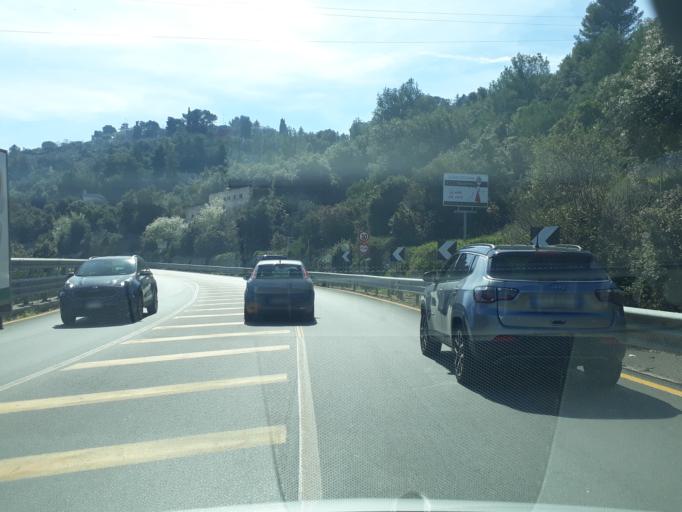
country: IT
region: Apulia
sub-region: Provincia di Brindisi
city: Lamie di Olimpie-Selva
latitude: 40.8107
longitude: 17.3449
